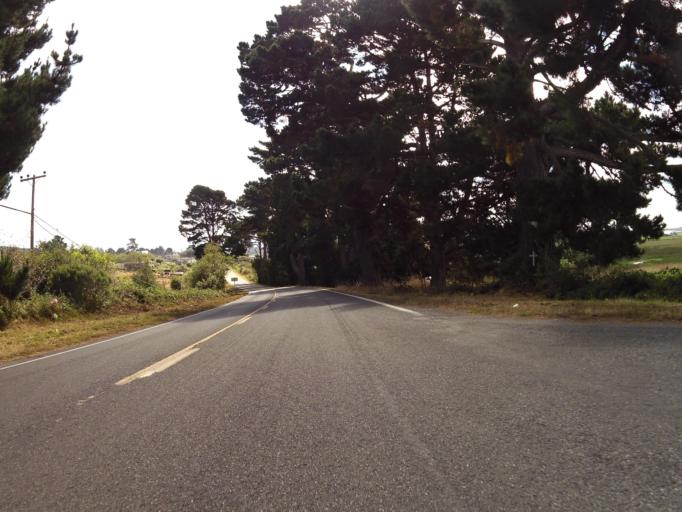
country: US
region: California
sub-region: Humboldt County
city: Ferndale
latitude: 40.6466
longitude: -124.2262
